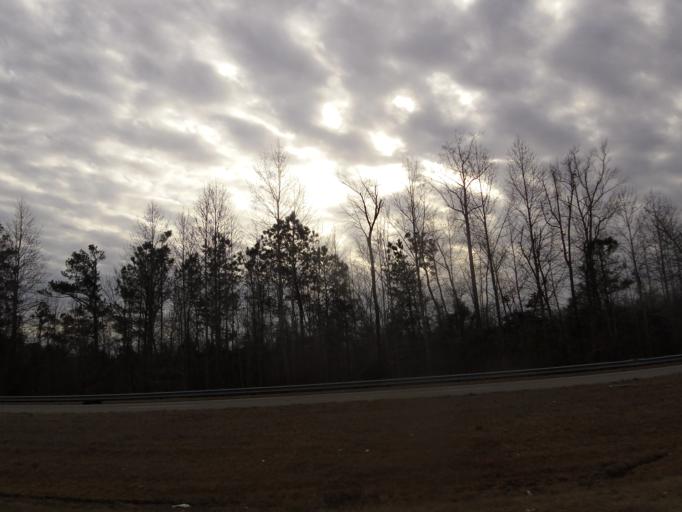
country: US
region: North Carolina
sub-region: Hertford County
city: Murfreesboro
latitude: 36.4352
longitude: -77.1355
